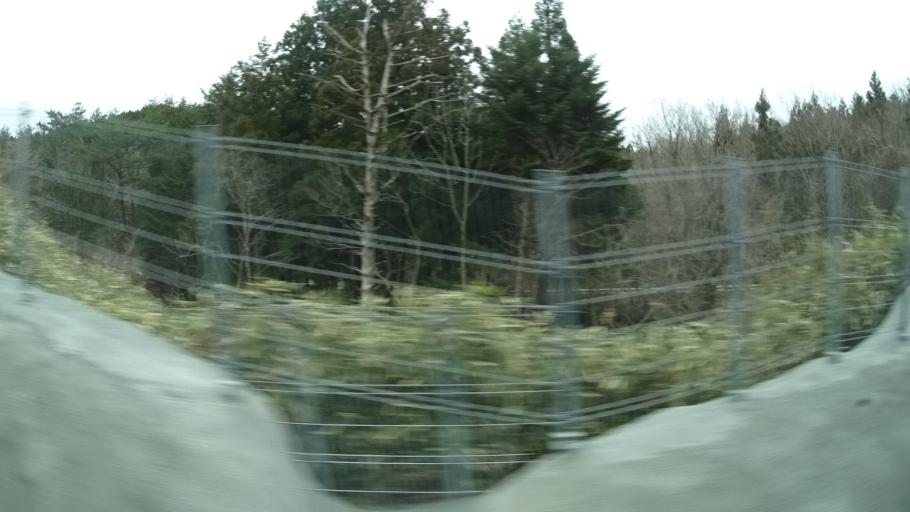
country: JP
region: Fukushima
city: Namie
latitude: 37.3751
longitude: 140.9909
